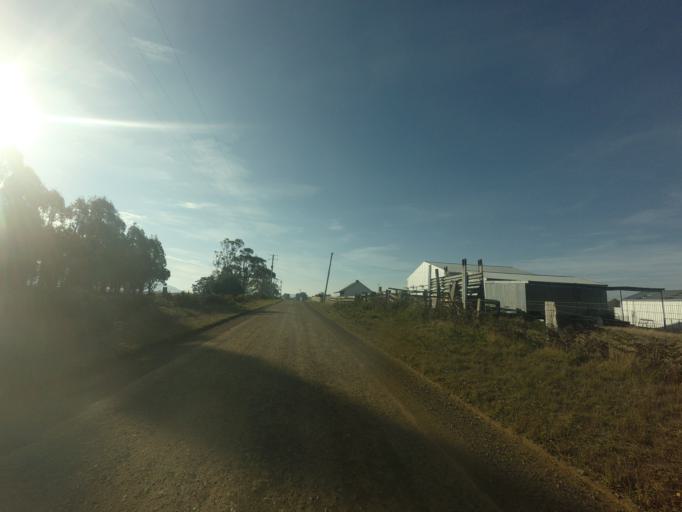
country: AU
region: Tasmania
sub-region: Brighton
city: Bridgewater
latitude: -42.4408
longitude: 147.3857
